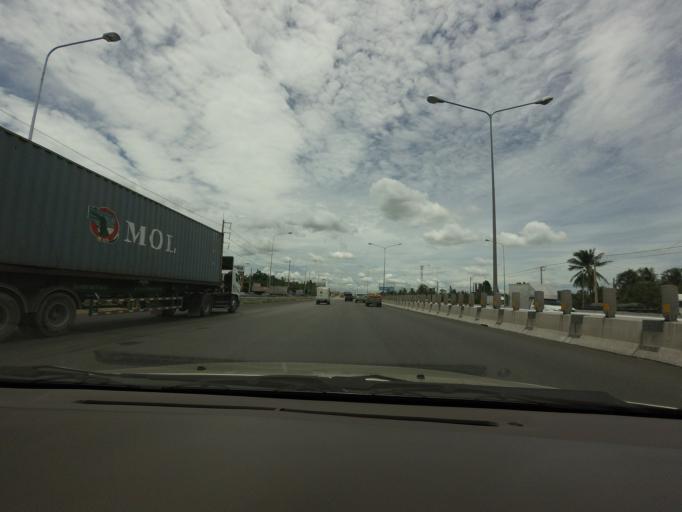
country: TH
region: Chon Buri
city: Si Racha
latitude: 13.2363
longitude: 100.9986
